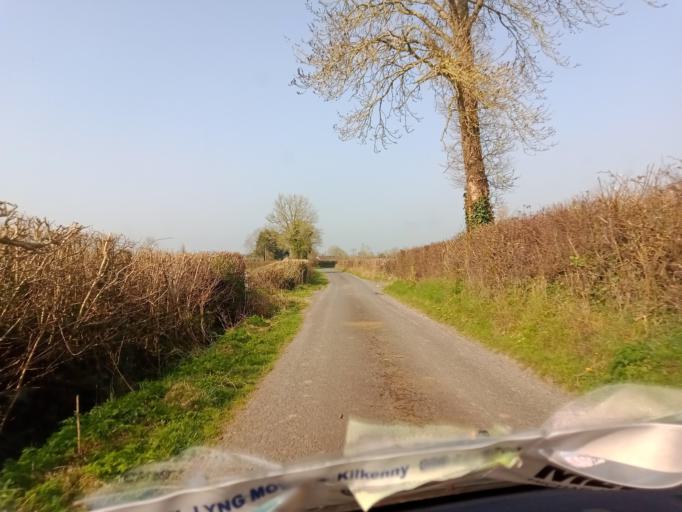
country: IE
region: Leinster
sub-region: Kilkenny
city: Callan
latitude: 52.5212
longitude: -7.4099
